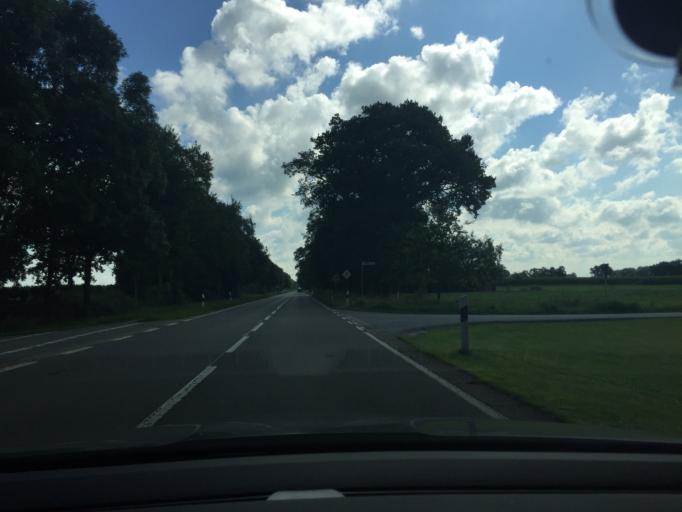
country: DE
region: Lower Saxony
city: Dunum
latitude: 53.5476
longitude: 7.6261
